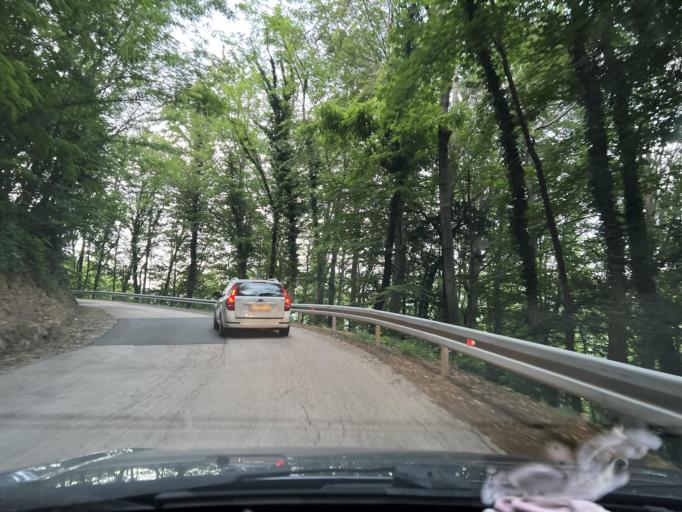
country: HR
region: Primorsko-Goranska
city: Marcelji
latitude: 45.3942
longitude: 14.4203
